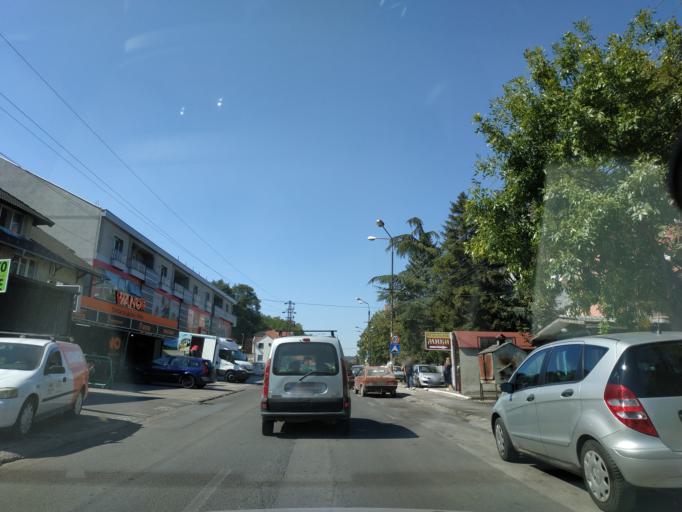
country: RS
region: Central Serbia
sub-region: Sumadijski Okrug
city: Arangelovac
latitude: 44.3025
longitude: 20.5676
